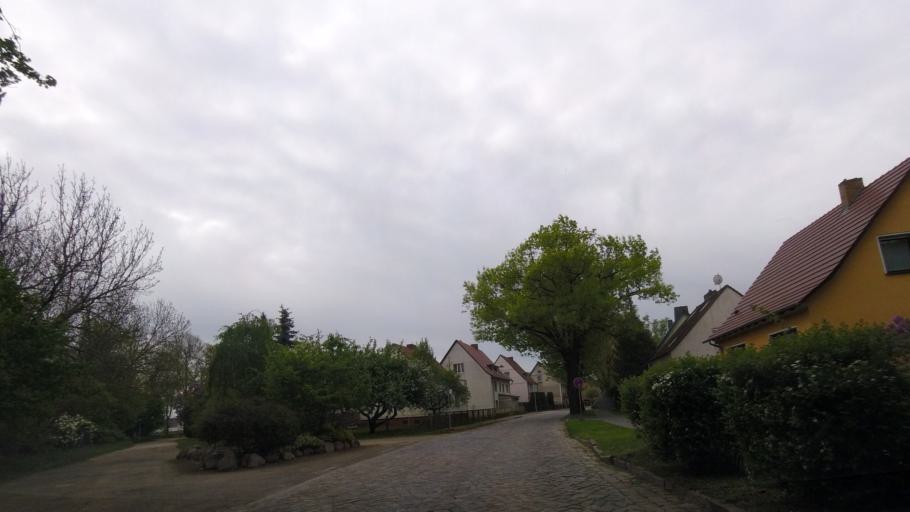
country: DE
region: Brandenburg
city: Dahme
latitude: 51.8723
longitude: 13.4345
